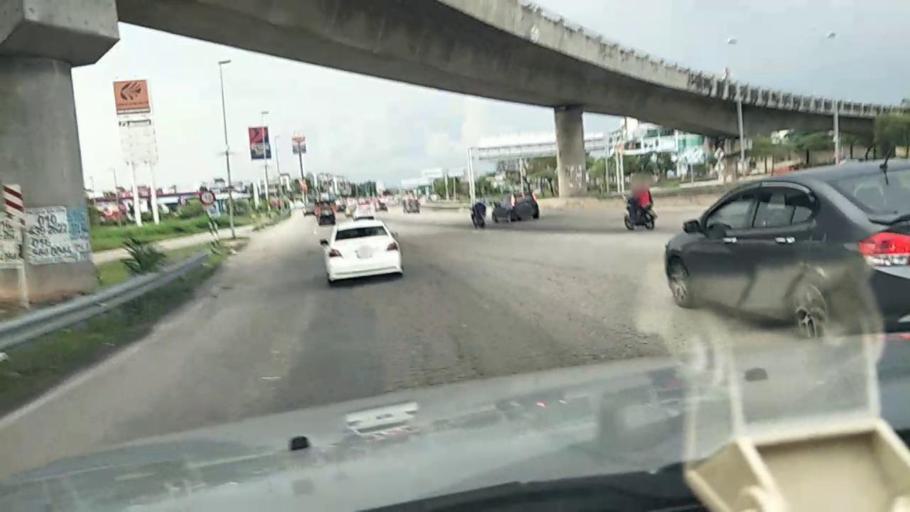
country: MY
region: Selangor
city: Klang
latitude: 3.1080
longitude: 101.4420
